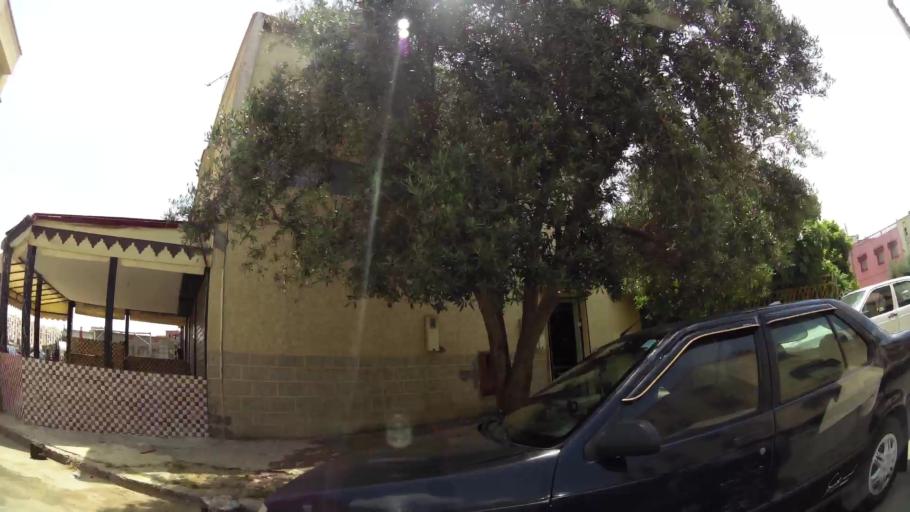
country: MA
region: Rabat-Sale-Zemmour-Zaer
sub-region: Khemisset
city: Tiflet
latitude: 34.0098
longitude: -6.5296
